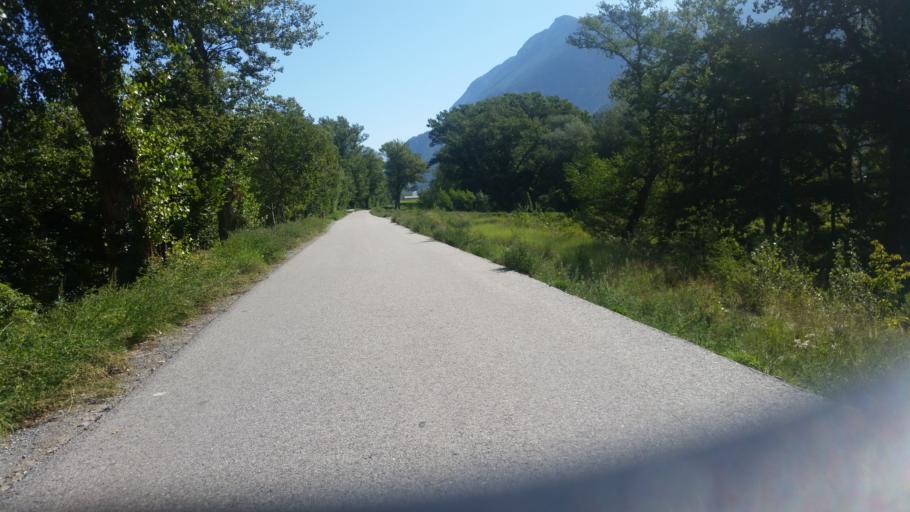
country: CH
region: Valais
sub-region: Sierre District
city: Chalais
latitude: 46.2750
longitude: 7.5010
